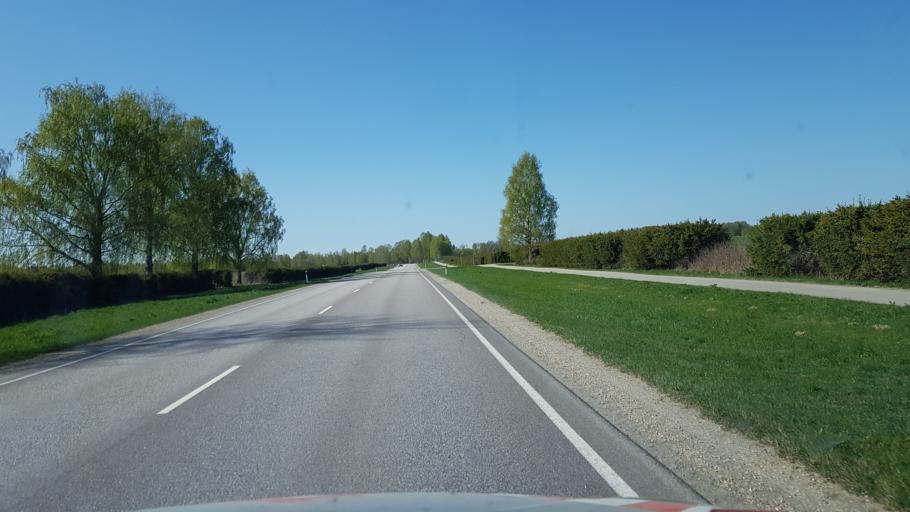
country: EE
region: Valgamaa
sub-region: Torva linn
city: Torva
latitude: 58.0239
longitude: 25.8677
